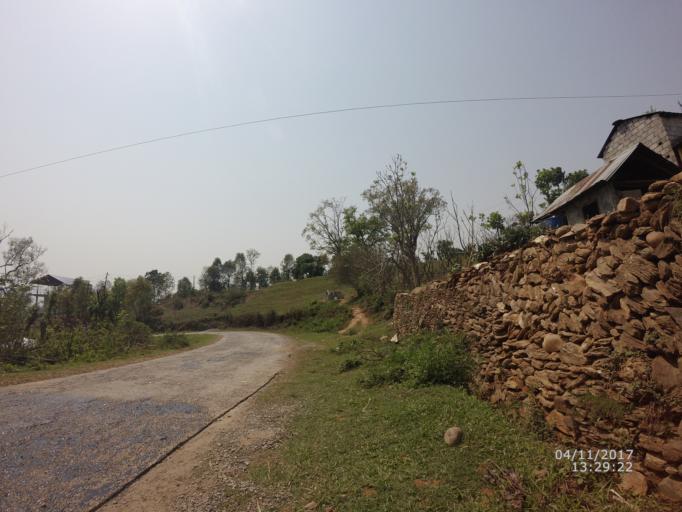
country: NP
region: Western Region
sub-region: Gandaki Zone
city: Pokhara
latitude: 28.1972
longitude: 84.0408
